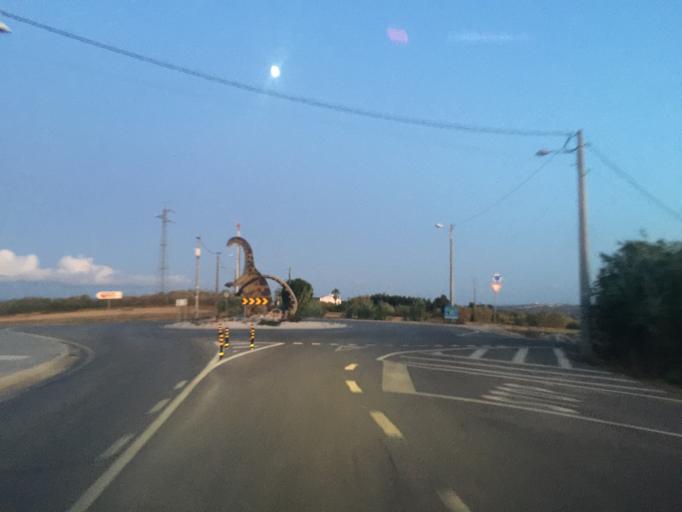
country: PT
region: Lisbon
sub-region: Lourinha
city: Lourinha
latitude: 39.2768
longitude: -9.2983
